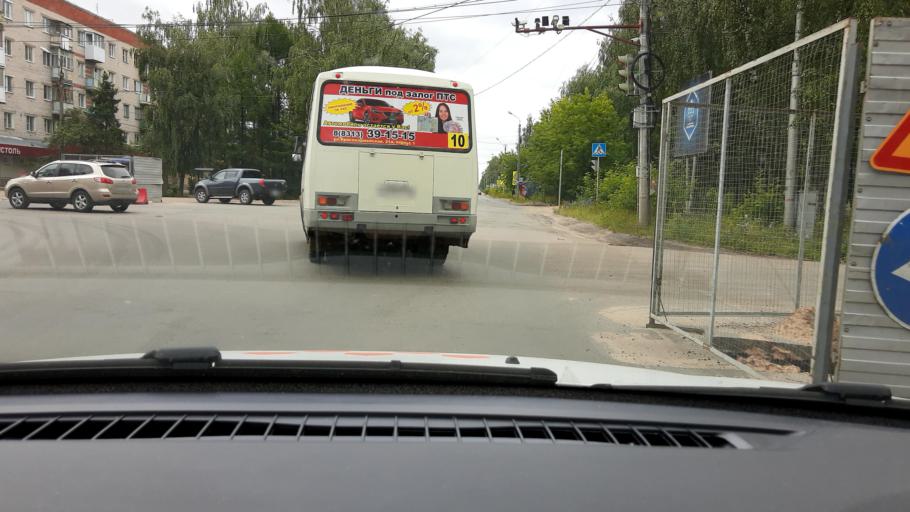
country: RU
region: Nizjnij Novgorod
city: Pyra
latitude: 56.2473
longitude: 43.3907
